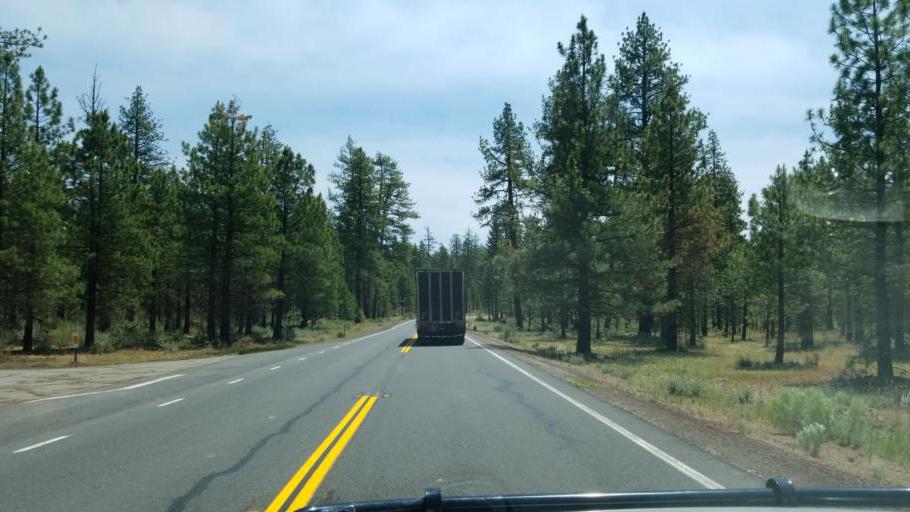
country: US
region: California
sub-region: Shasta County
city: Burney
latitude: 40.6710
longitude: -121.3632
